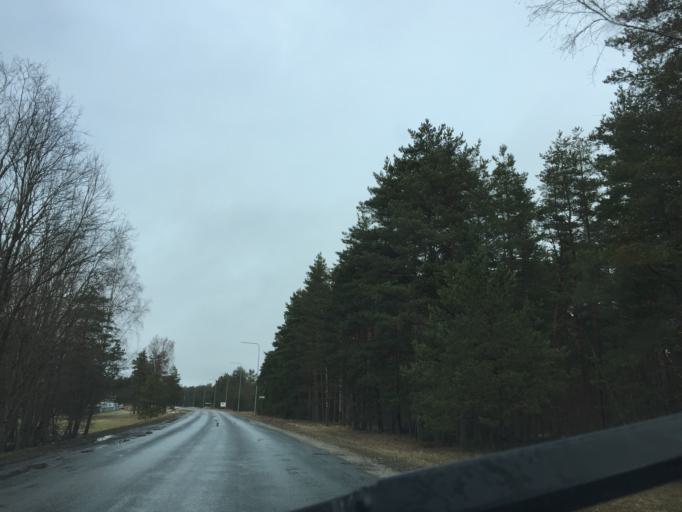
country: EE
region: Laeaene
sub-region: Haapsalu linn
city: Haapsalu
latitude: 58.9186
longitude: 23.5495
